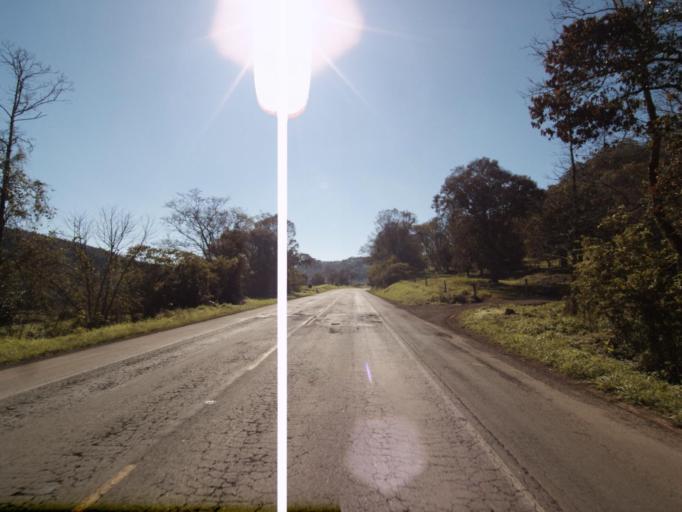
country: BR
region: Rio Grande do Sul
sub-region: Frederico Westphalen
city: Frederico Westphalen
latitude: -27.0263
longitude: -53.2327
